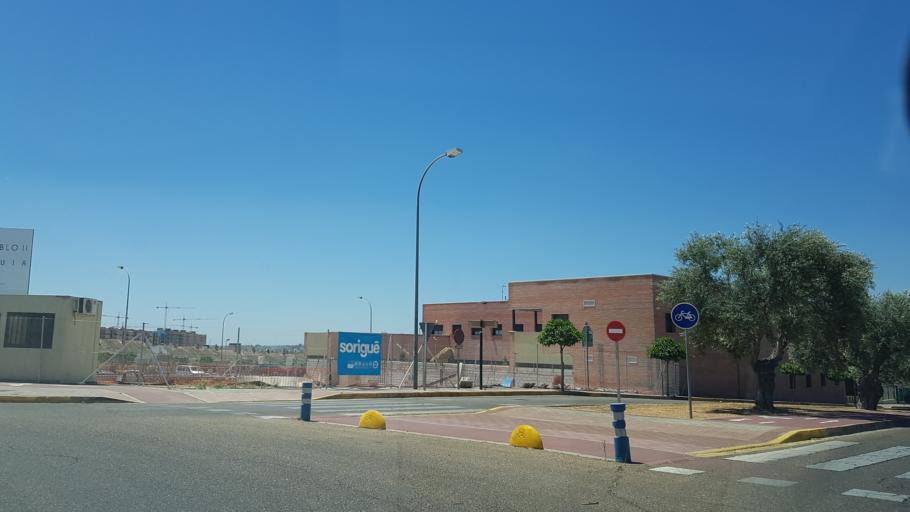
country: ES
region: Andalusia
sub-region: Provincia de Sevilla
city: Dos Hermanas
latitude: 37.3257
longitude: -5.9268
